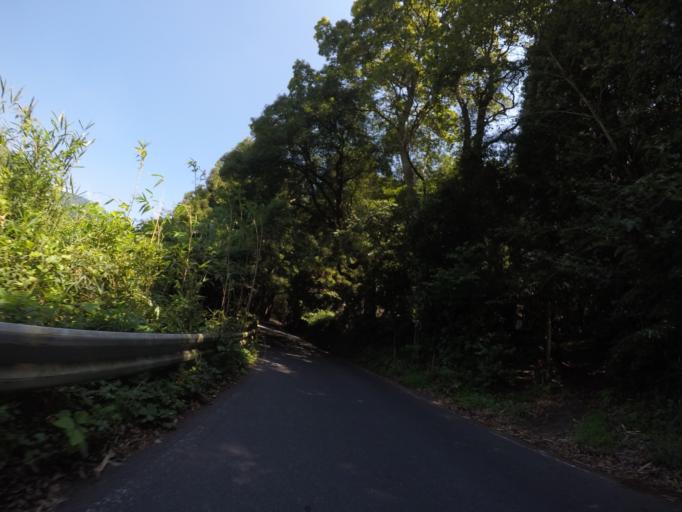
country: JP
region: Shizuoka
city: Fujinomiya
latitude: 35.2705
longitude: 138.5666
